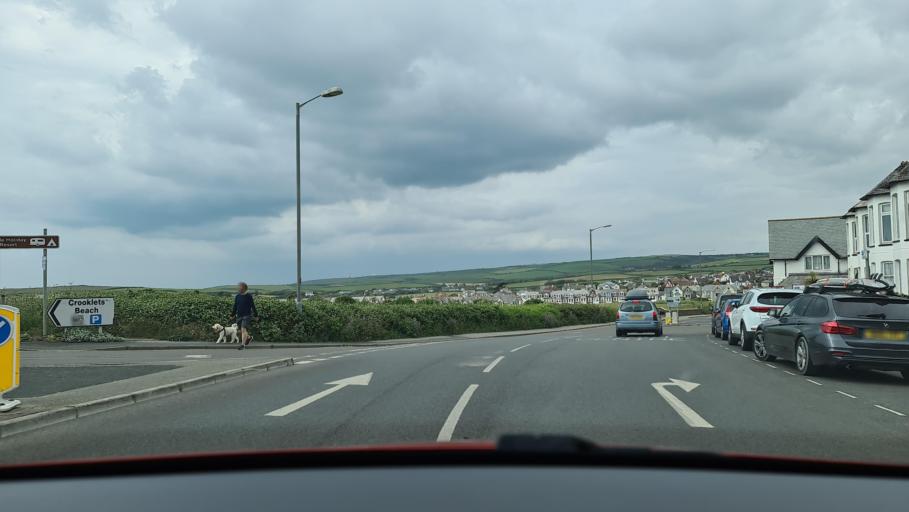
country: GB
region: England
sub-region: Cornwall
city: Flexbury
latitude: 50.8318
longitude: -4.5460
